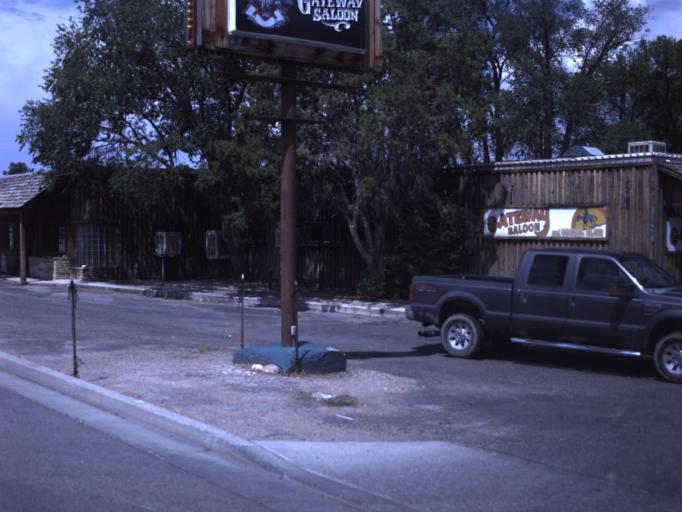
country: US
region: Utah
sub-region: Uintah County
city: Vernal
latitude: 40.4560
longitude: -109.5134
